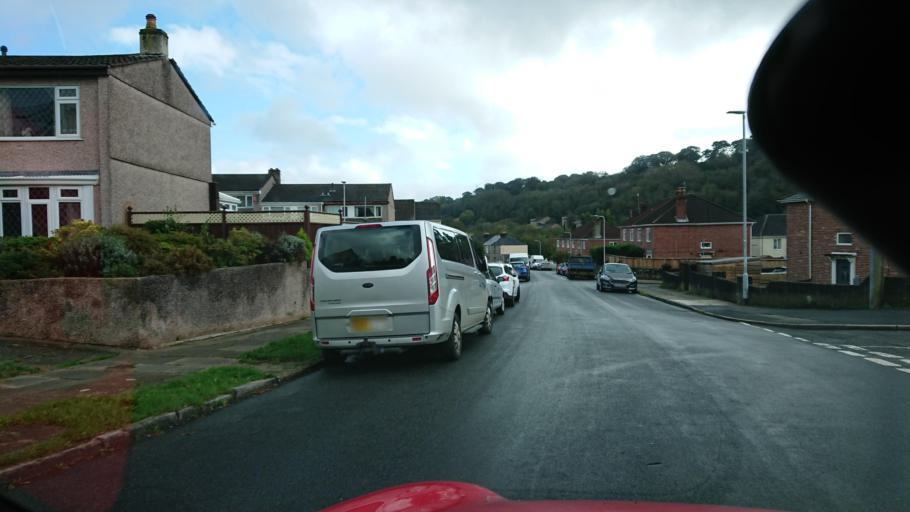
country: GB
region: England
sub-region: Plymouth
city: Plymouth
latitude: 50.3970
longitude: -4.1108
